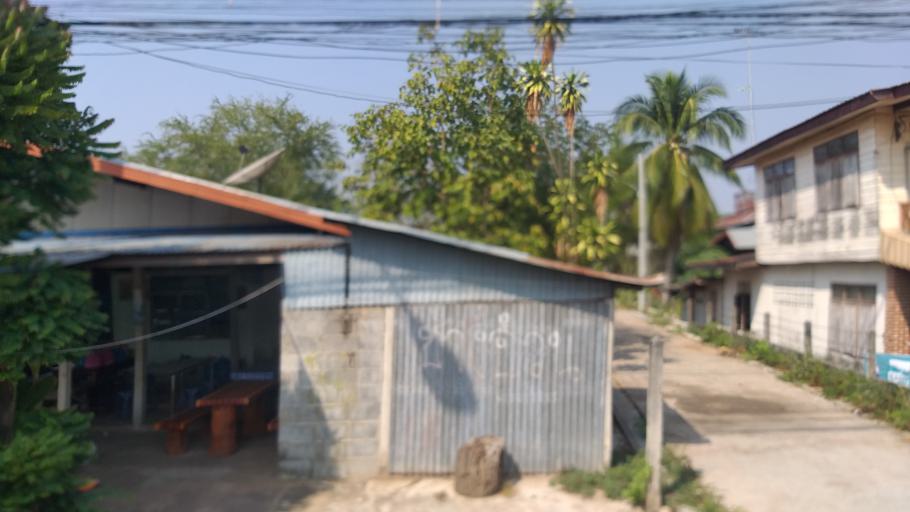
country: TH
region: Changwat Udon Thani
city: Nong Han
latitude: 17.3629
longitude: 103.1001
